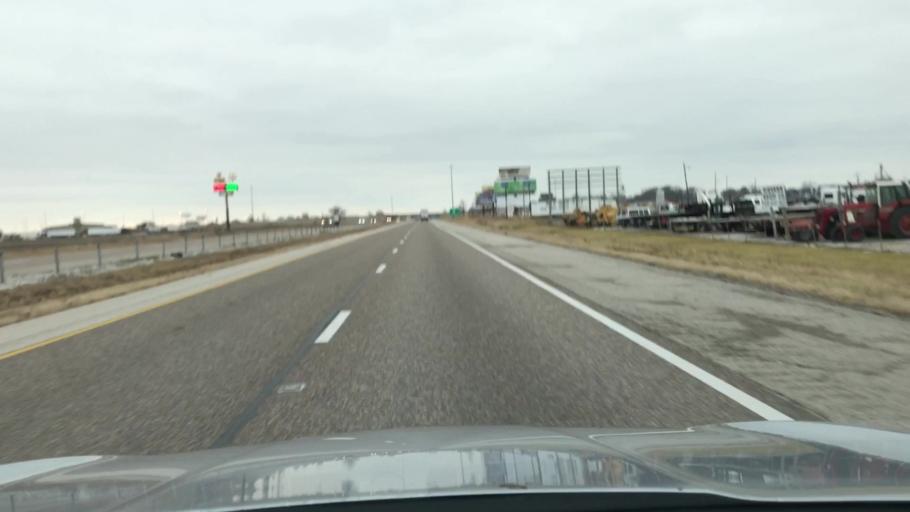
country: US
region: Illinois
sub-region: Madison County
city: Worden
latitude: 38.8961
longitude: -89.8338
